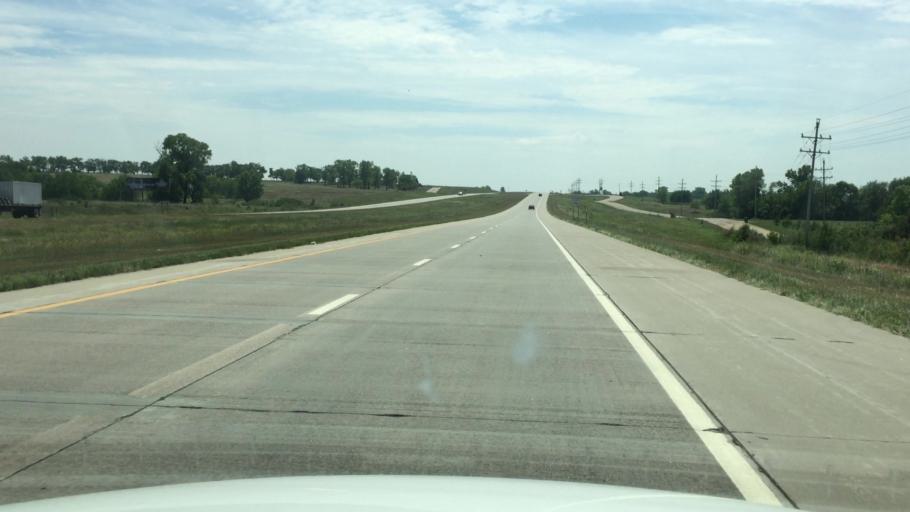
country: US
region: Kansas
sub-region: Shawnee County
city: Silver Lake
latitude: 39.2445
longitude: -95.7197
